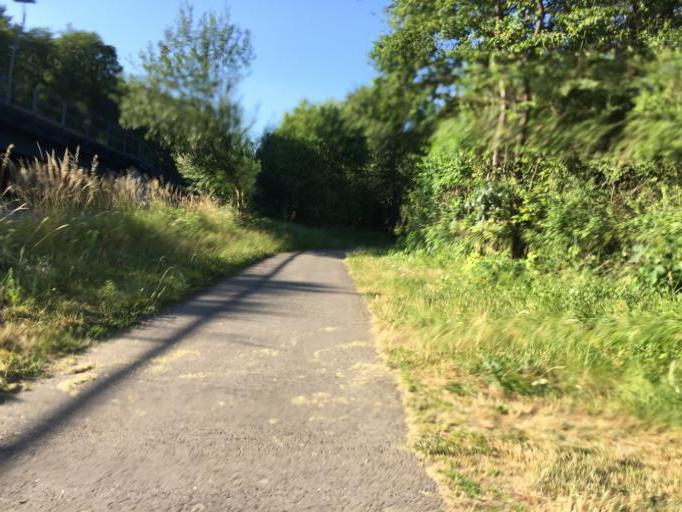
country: DE
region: Rheinland-Pfalz
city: Bilkheim
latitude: 50.4946
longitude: 7.9440
